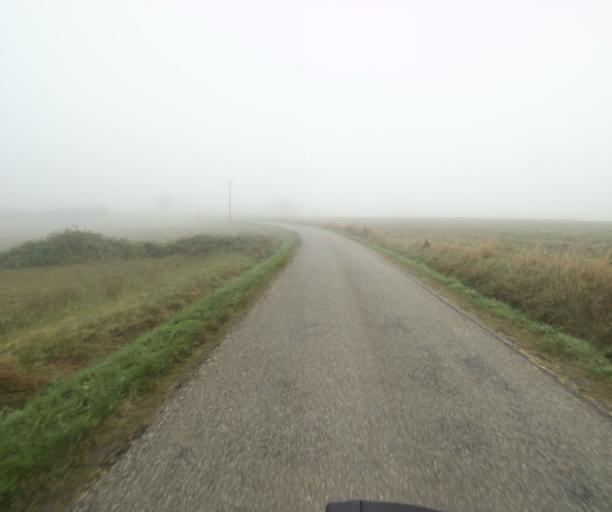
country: FR
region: Midi-Pyrenees
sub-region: Departement de la Haute-Garonne
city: Villemur-sur-Tarn
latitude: 43.9063
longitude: 1.4853
